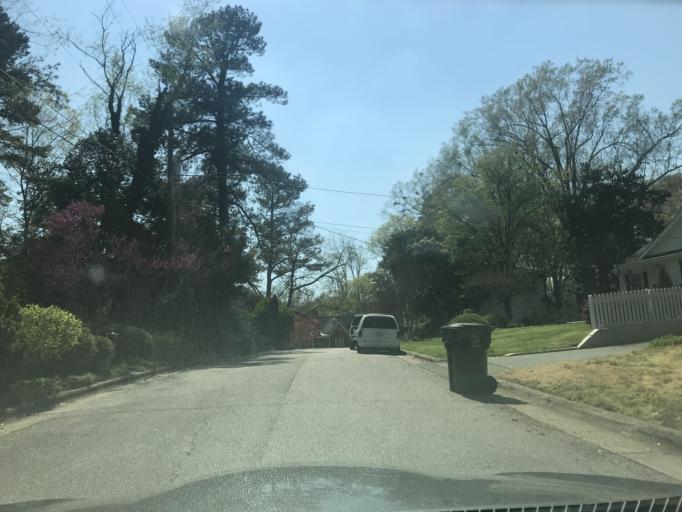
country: US
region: North Carolina
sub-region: Wake County
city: West Raleigh
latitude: 35.8143
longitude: -78.6403
